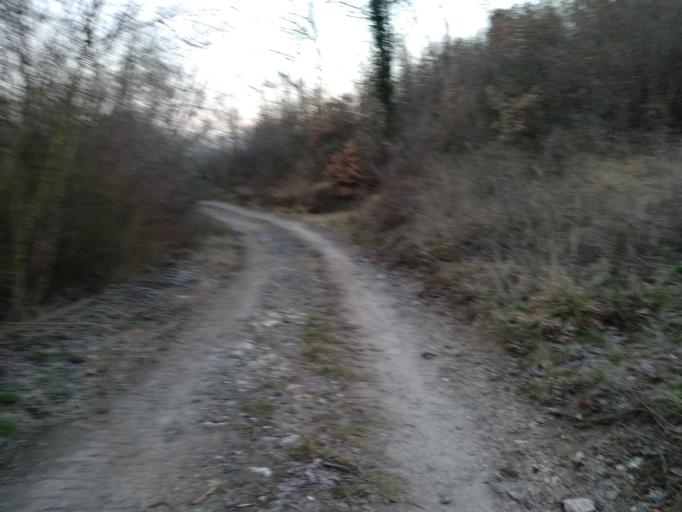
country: IT
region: Veneto
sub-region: Provincia di Padova
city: Battaglia Terme
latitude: 45.3016
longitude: 11.7745
